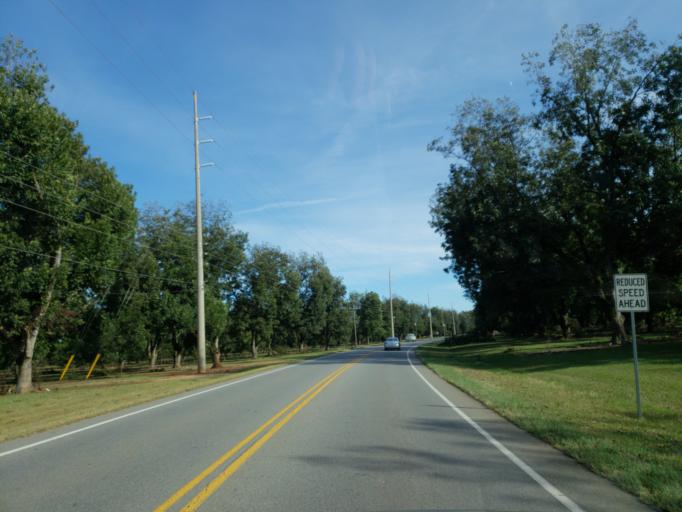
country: US
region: Georgia
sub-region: Peach County
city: Fort Valley
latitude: 32.5737
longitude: -83.8922
